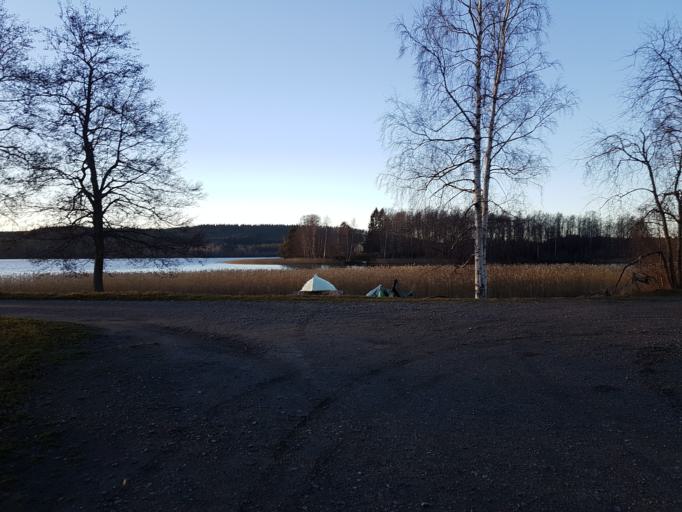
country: FI
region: Northern Savo
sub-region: Kuopio
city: Kuopio
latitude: 62.9301
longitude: 27.6246
